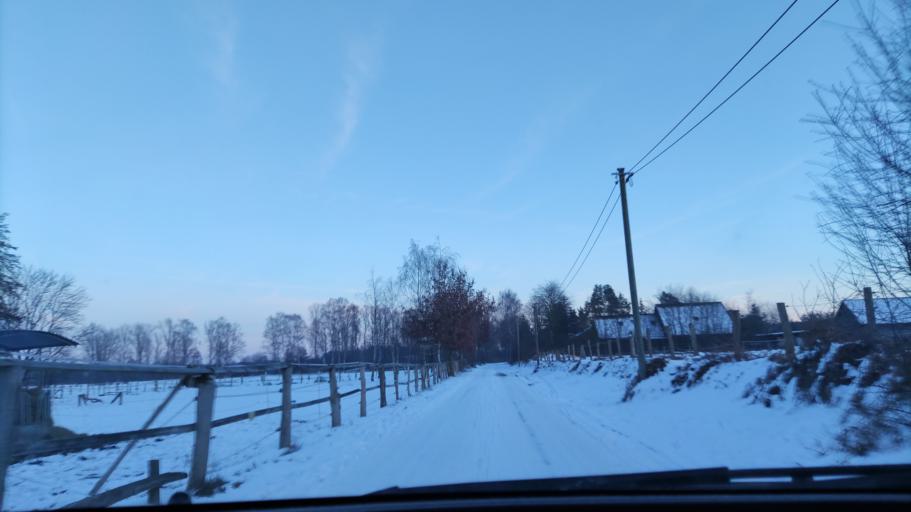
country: DE
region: Lower Saxony
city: Neetze
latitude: 53.2968
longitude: 10.6676
